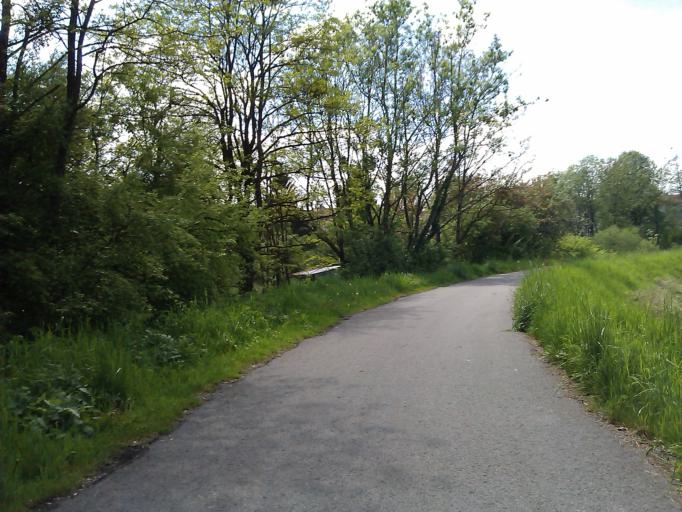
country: FR
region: Franche-Comte
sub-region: Departement du Doubs
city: Voujeaucourt
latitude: 47.4767
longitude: 6.7606
